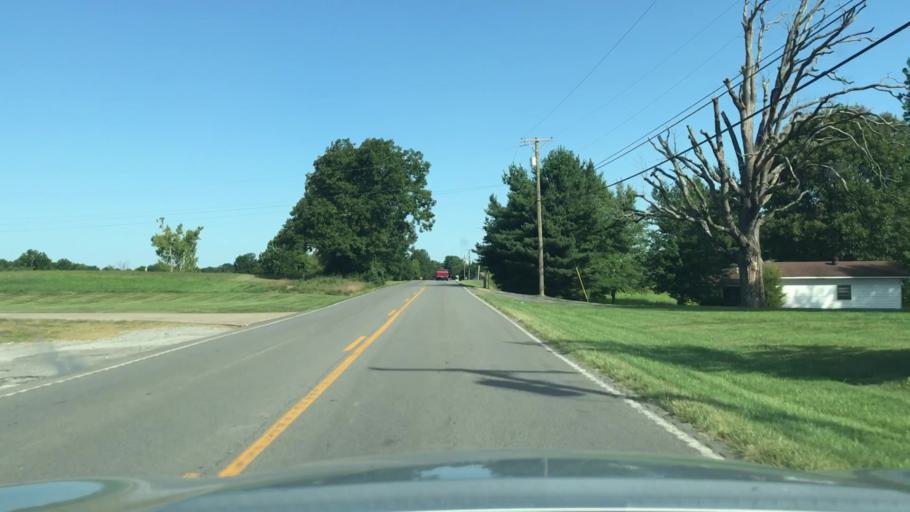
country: US
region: Kentucky
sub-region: Muhlenberg County
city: Greenville
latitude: 37.1835
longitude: -87.1575
